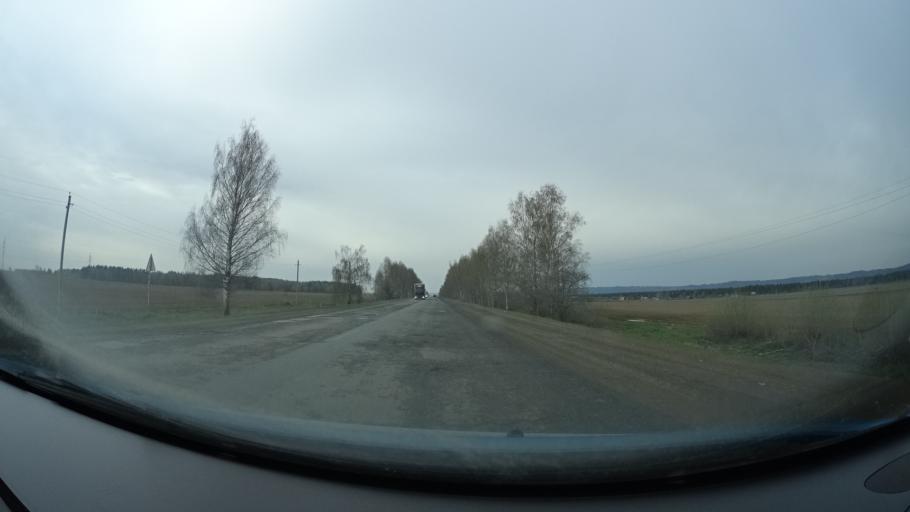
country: RU
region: Perm
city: Ust'-Kachka
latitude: 58.0560
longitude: 55.6037
